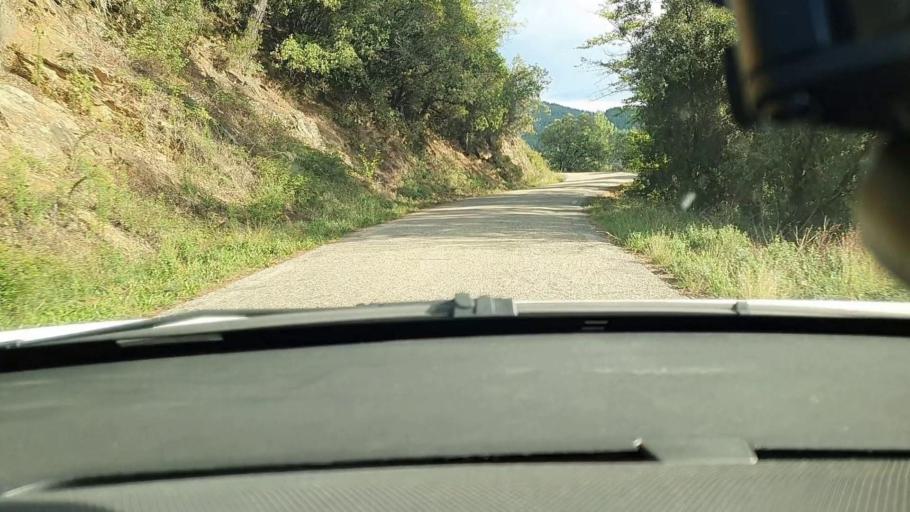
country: FR
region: Languedoc-Roussillon
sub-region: Departement du Gard
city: Besseges
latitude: 44.3200
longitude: 4.0450
